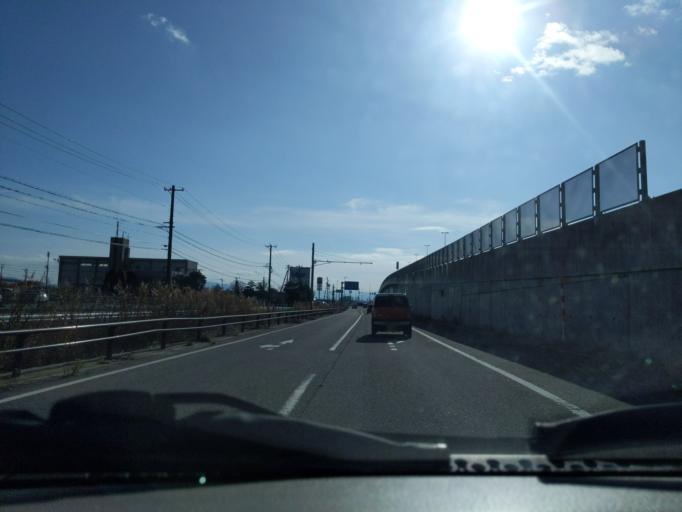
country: JP
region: Niigata
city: Kameda-honcho
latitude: 37.8715
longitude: 139.0869
